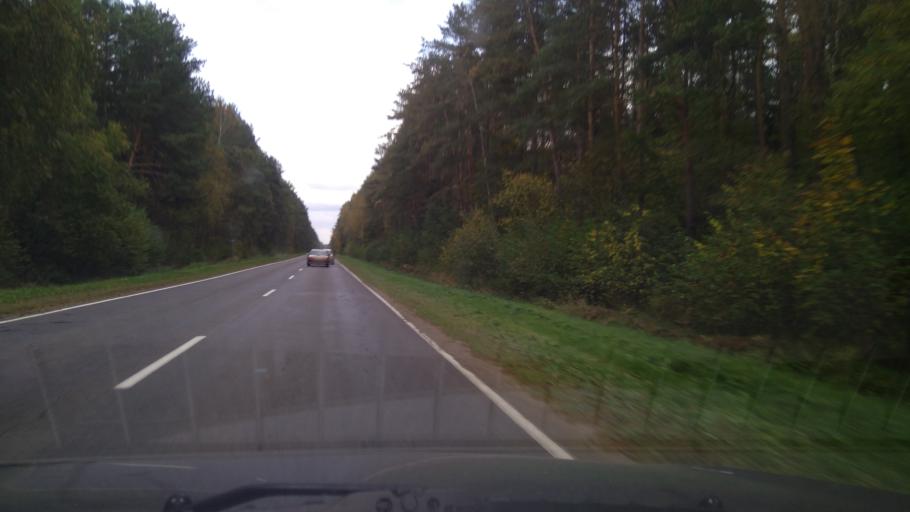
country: BY
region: Minsk
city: Druzhny
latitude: 53.6255
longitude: 27.8710
